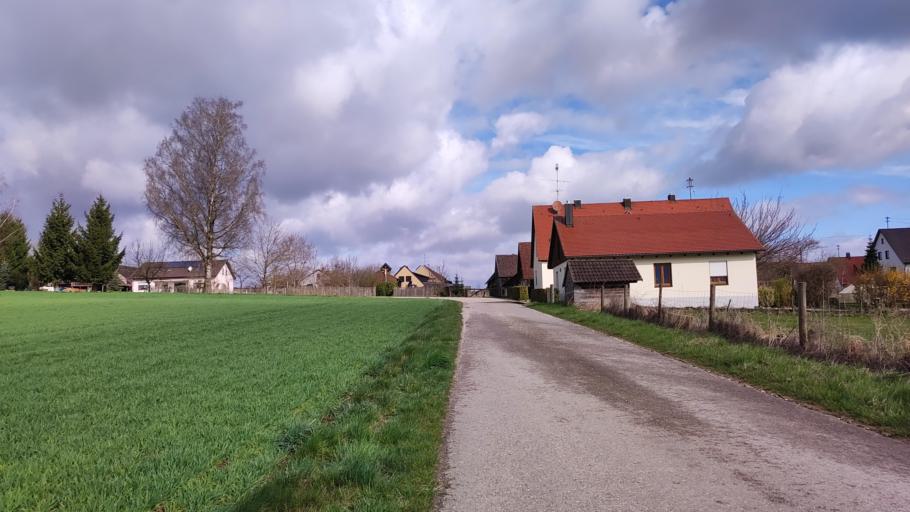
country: DE
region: Bavaria
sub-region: Swabia
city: Altenmunster
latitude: 48.4442
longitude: 10.5883
